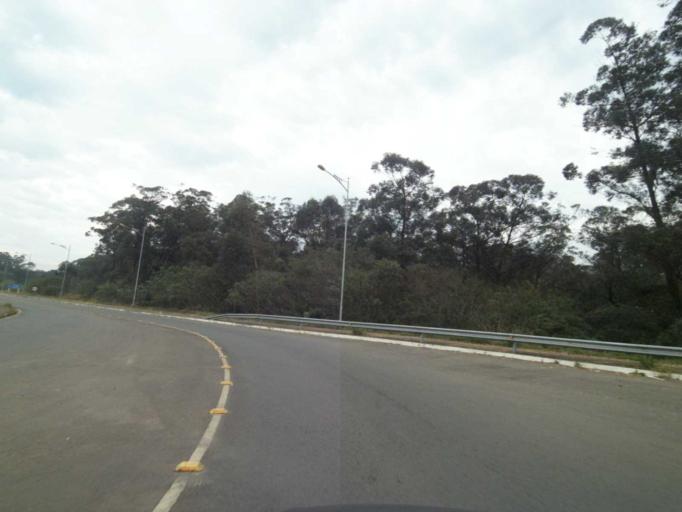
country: BR
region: Rio Grande do Sul
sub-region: Sao Leopoldo
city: Sao Leopoldo
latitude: -29.7847
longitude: -51.1649
